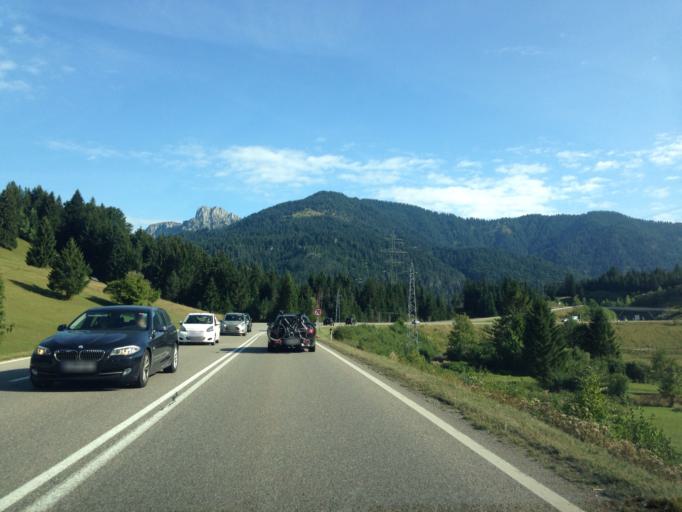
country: AT
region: Tyrol
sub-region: Politischer Bezirk Reutte
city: Breitenwang
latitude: 47.4873
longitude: 10.7432
